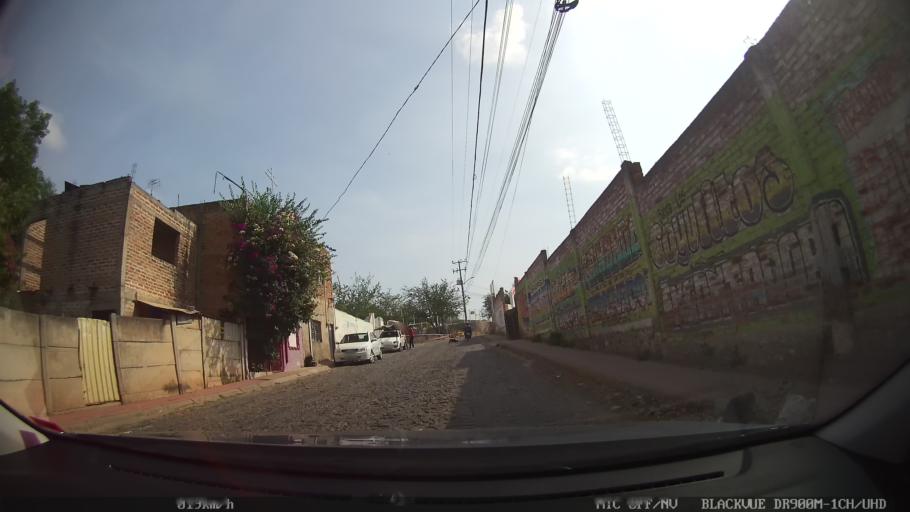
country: MX
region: Jalisco
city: Tonala
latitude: 20.6320
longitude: -103.2378
